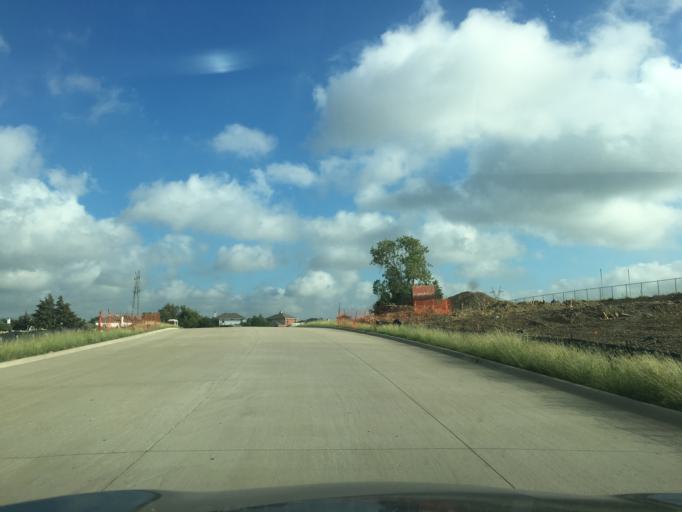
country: US
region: Texas
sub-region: Dallas County
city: Sachse
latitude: 32.9615
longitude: -96.5913
